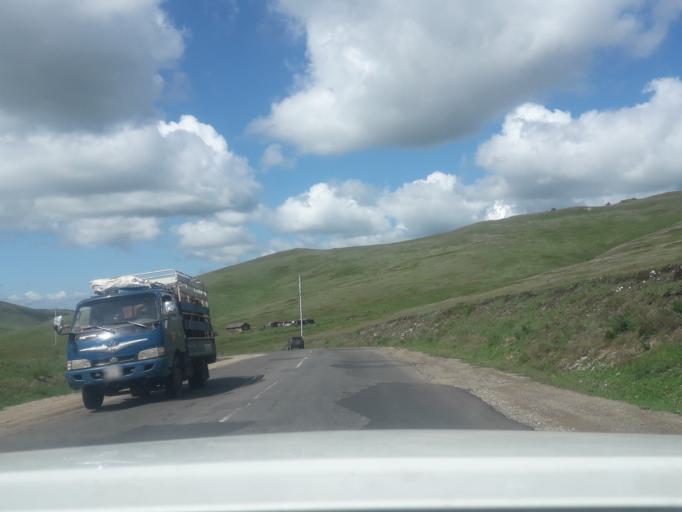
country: MN
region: Central Aimak
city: Ihsueuej
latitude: 48.1379
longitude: 106.4232
